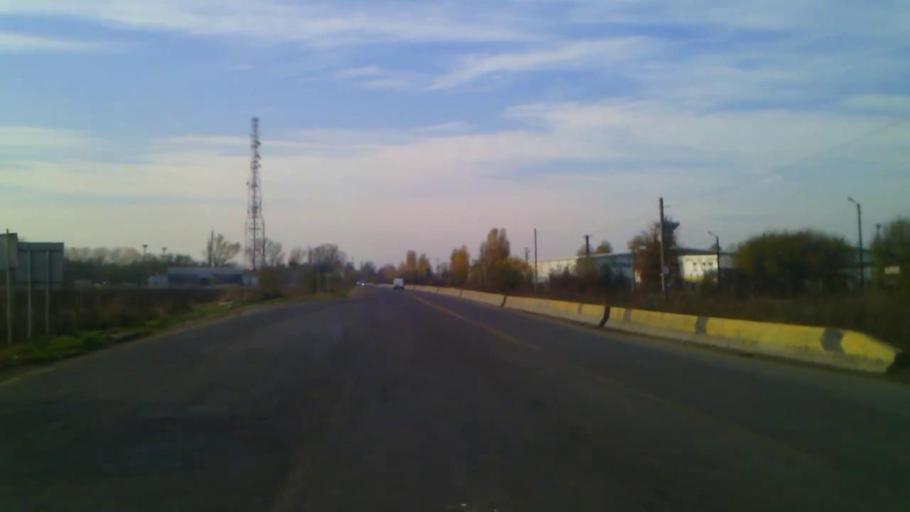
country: RO
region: Ilfov
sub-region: Comuna Berceni
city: Berceni
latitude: 44.3403
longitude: 26.1651
